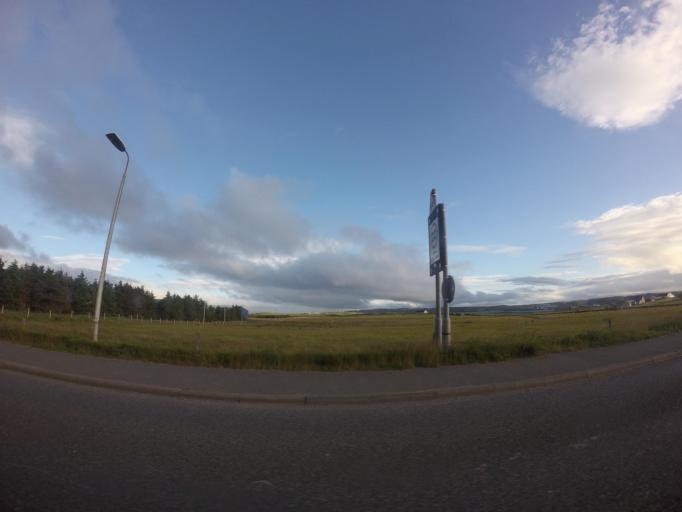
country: GB
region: Scotland
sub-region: Eilean Siar
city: Stornoway
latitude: 58.2032
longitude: -6.3459
